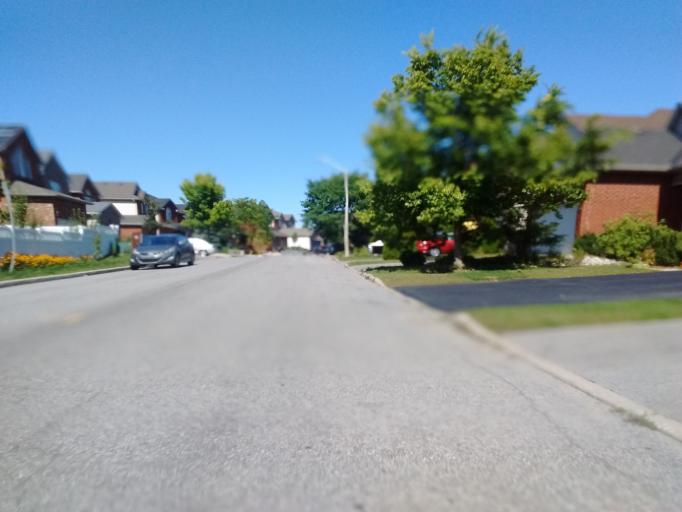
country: CA
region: Ontario
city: Ottawa
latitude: 45.4384
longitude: -75.6314
